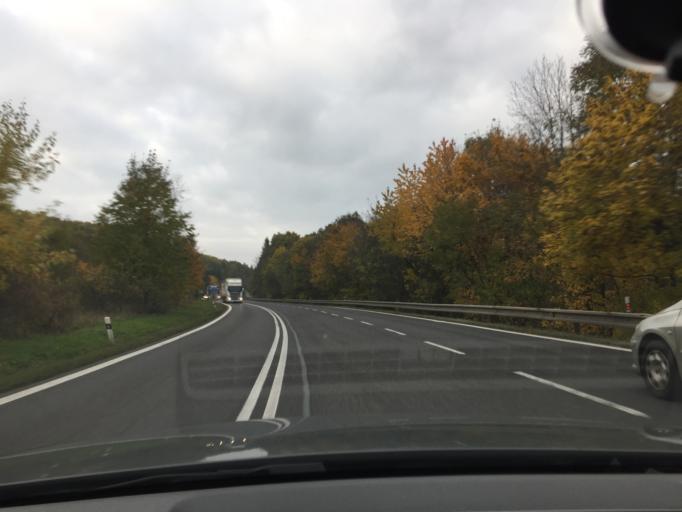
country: CZ
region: Ustecky
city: Velemin
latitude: 50.5551
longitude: 13.9657
